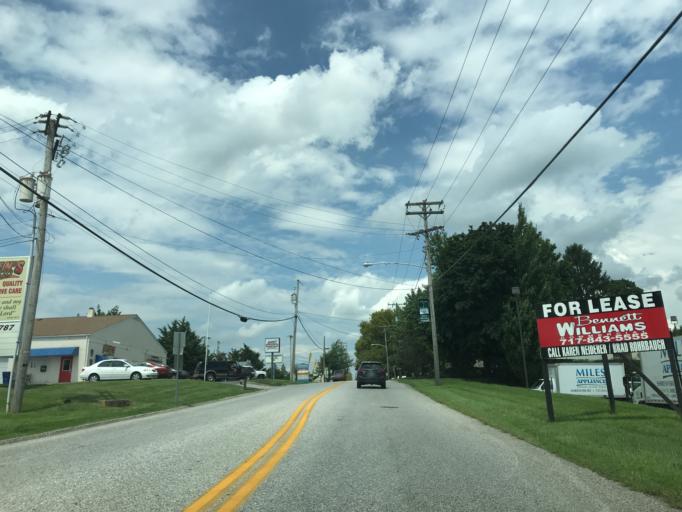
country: US
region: Pennsylvania
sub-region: York County
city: Shrewsbury
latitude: 39.7540
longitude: -76.6776
